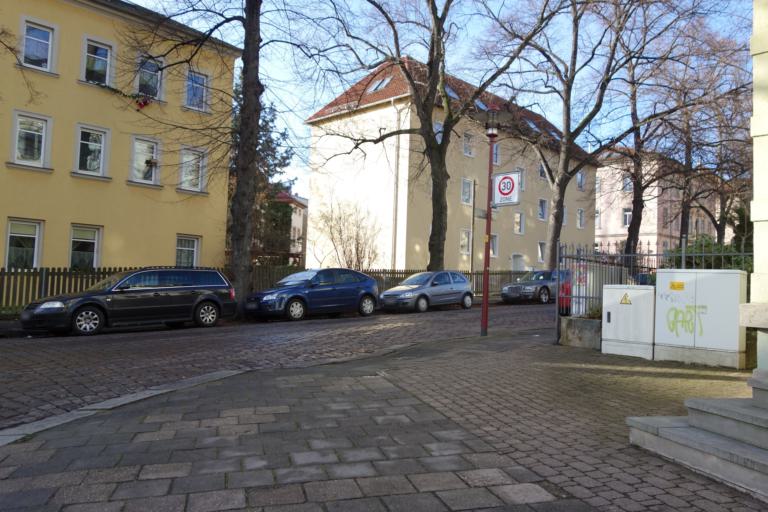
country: DE
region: Saxony
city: Radebeul
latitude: 51.0611
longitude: 13.6766
